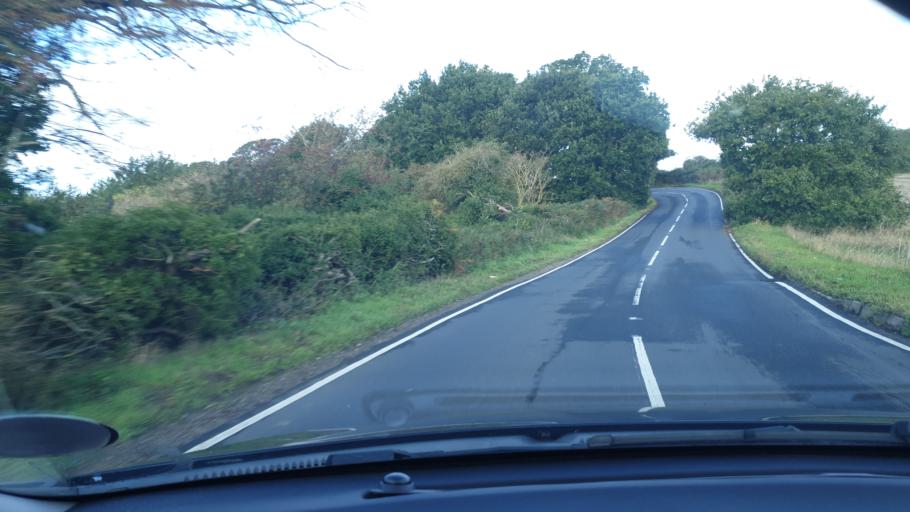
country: GB
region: England
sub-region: Essex
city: Mistley
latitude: 51.9400
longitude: 1.1017
